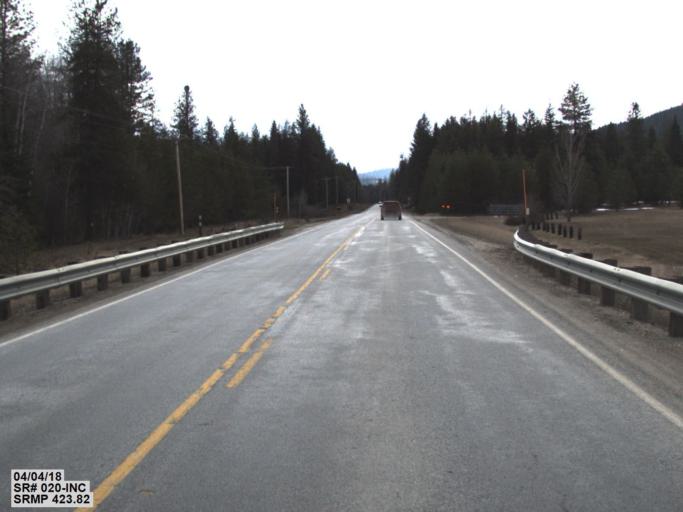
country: US
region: Washington
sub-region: Pend Oreille County
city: Newport
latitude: 48.2742
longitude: -117.2632
